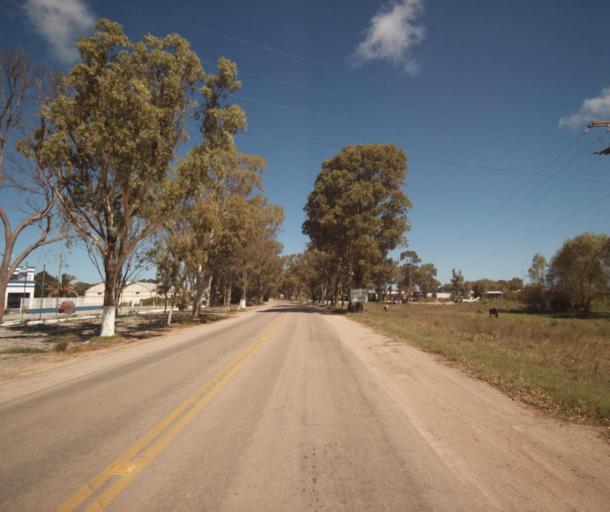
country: BR
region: Rio Grande do Sul
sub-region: Chui
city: Chui
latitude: -33.6847
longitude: -53.4488
